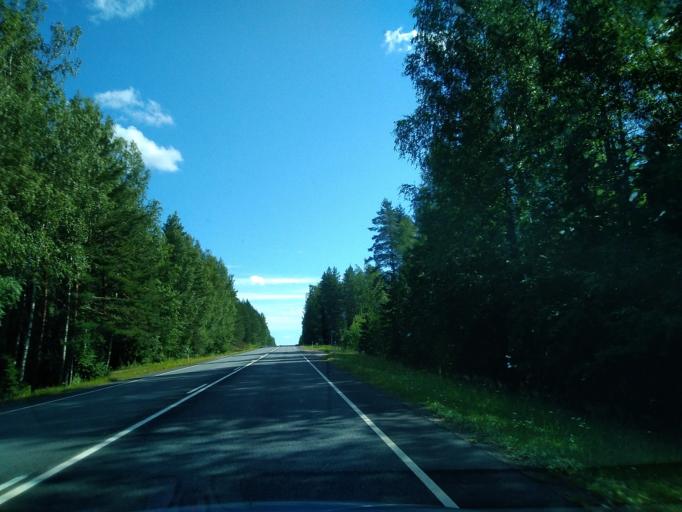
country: FI
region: Haeme
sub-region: Haemeenlinna
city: Renko
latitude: 60.8406
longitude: 24.1013
